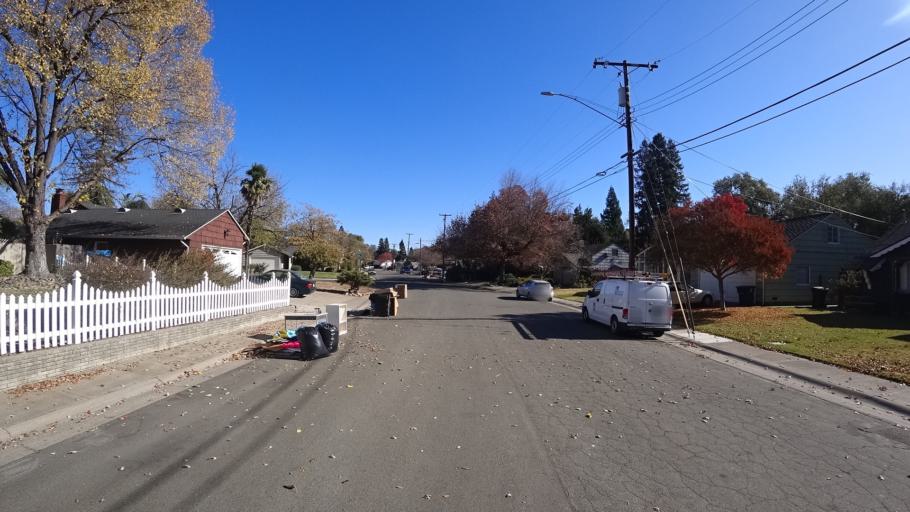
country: US
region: California
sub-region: Sacramento County
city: Foothill Farms
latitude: 38.6744
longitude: -121.3197
